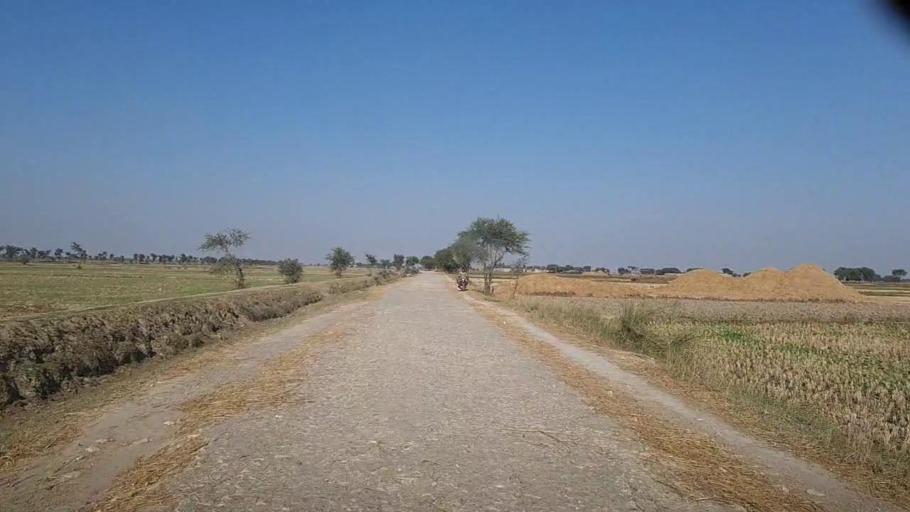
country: PK
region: Sindh
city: Thul
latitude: 28.3499
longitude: 68.7623
